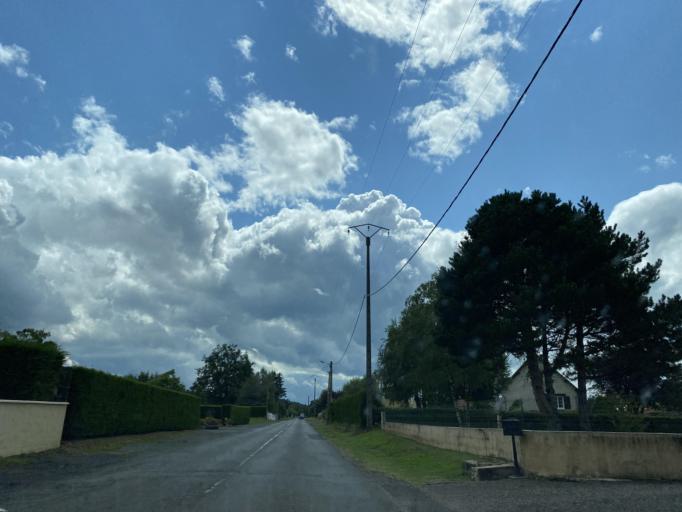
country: FR
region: Auvergne
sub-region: Departement du Puy-de-Dome
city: Peschadoires
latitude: 45.8310
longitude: 3.4880
